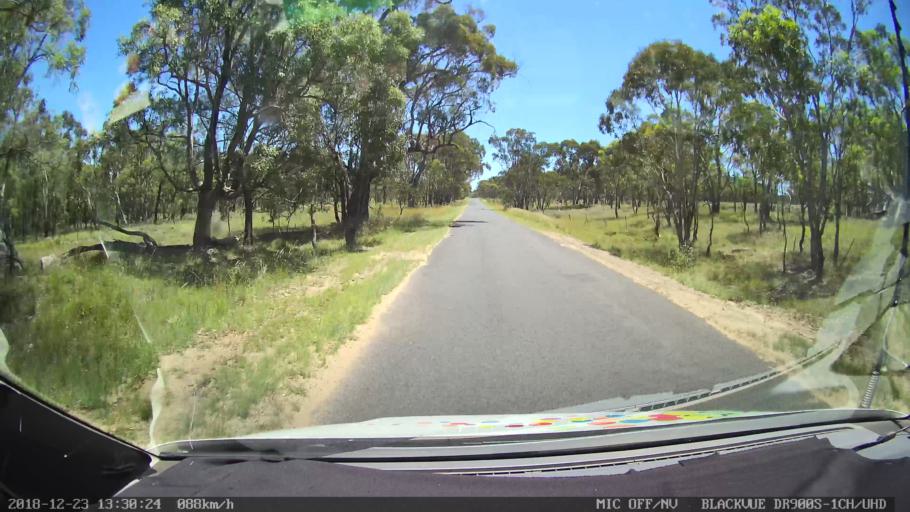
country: AU
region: New South Wales
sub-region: Armidale Dumaresq
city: Armidale
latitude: -30.4648
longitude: 151.3204
